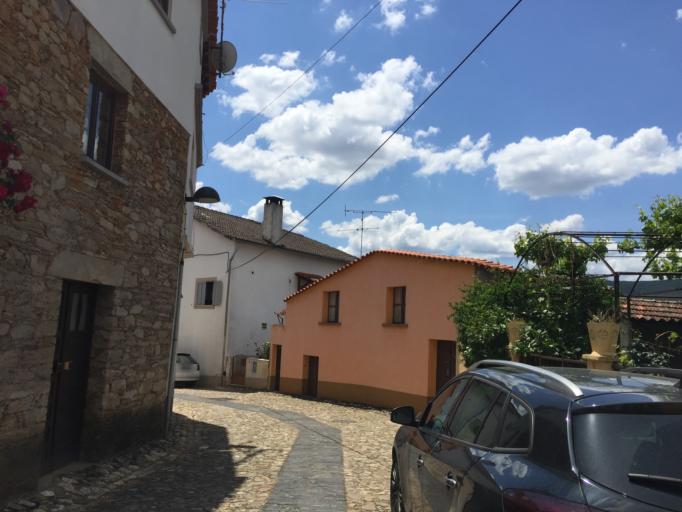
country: PT
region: Coimbra
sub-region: Pampilhosa da Serra
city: Pampilhosa da Serra
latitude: 40.0671
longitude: -7.8001
